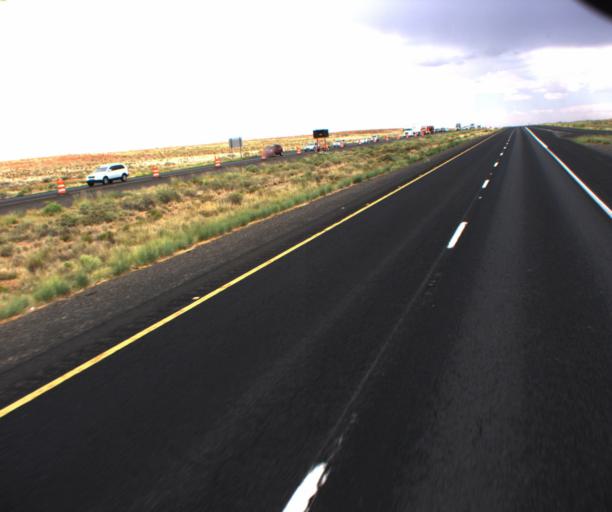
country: US
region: Arizona
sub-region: Coconino County
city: LeChee
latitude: 35.1169
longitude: -111.0881
